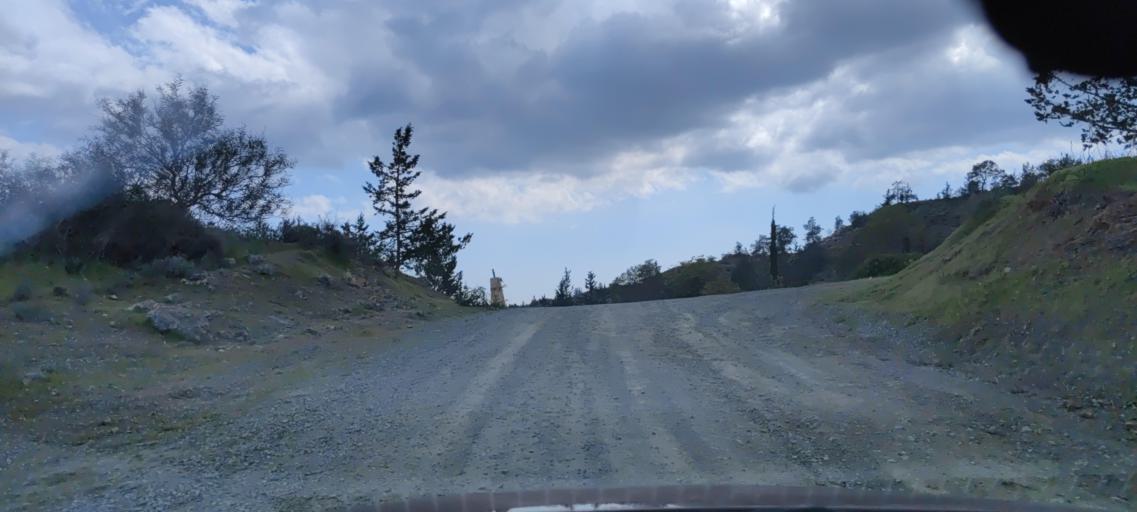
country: CY
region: Larnaka
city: Kornos
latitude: 34.9093
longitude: 33.4009
